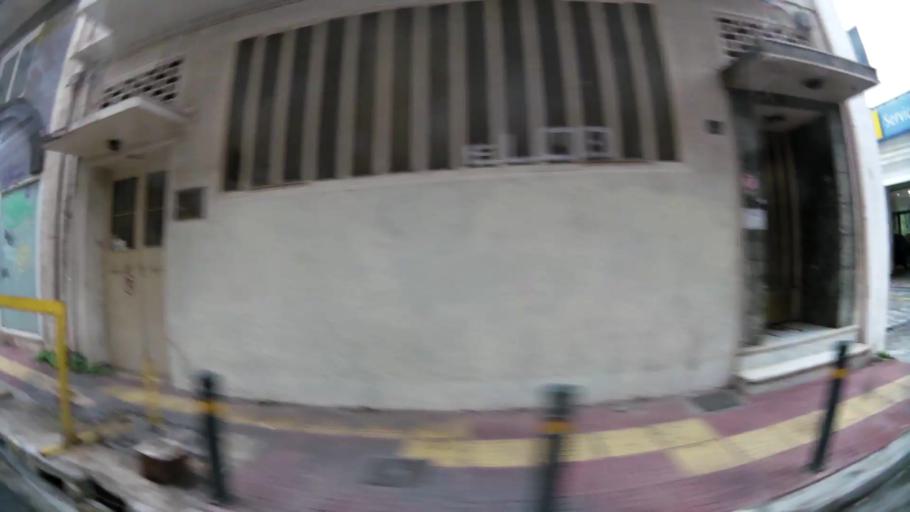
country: GR
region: Attica
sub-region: Nomarchia Athinas
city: Ymittos
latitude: 37.9612
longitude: 23.7397
